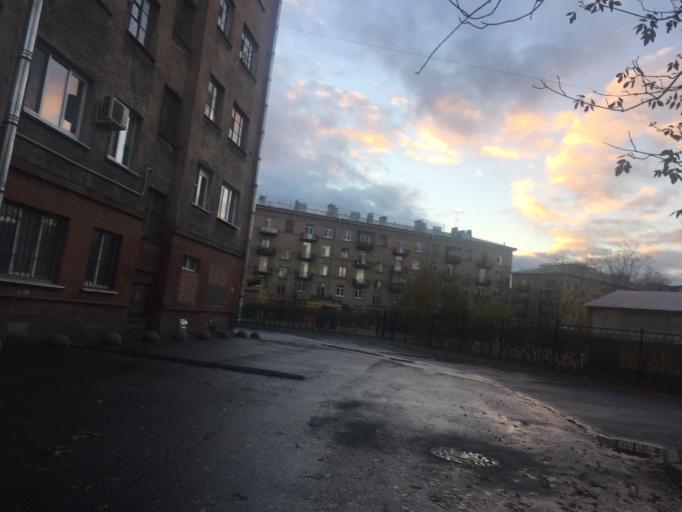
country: RU
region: St.-Petersburg
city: Obukhovo
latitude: 59.8788
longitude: 30.4331
